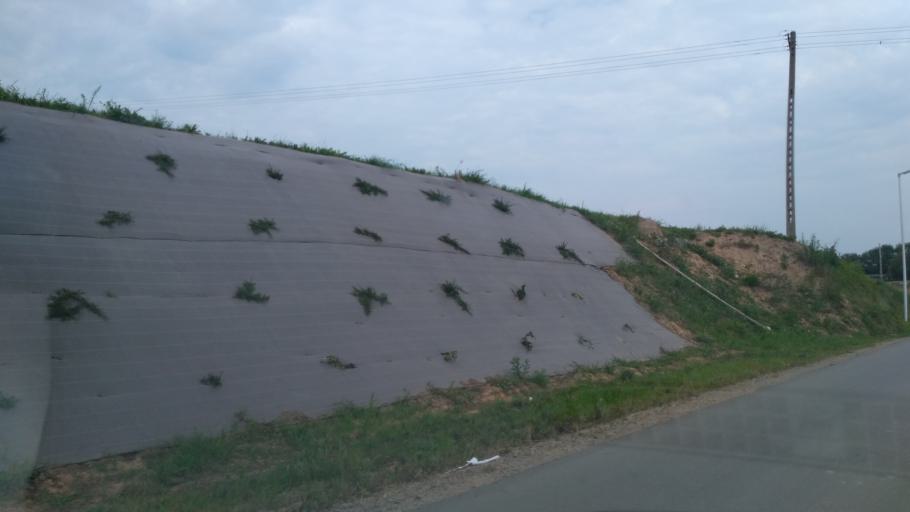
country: PL
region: Subcarpathian Voivodeship
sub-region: Powiat jaroslawski
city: Pawlosiow
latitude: 49.9679
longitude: 22.6291
